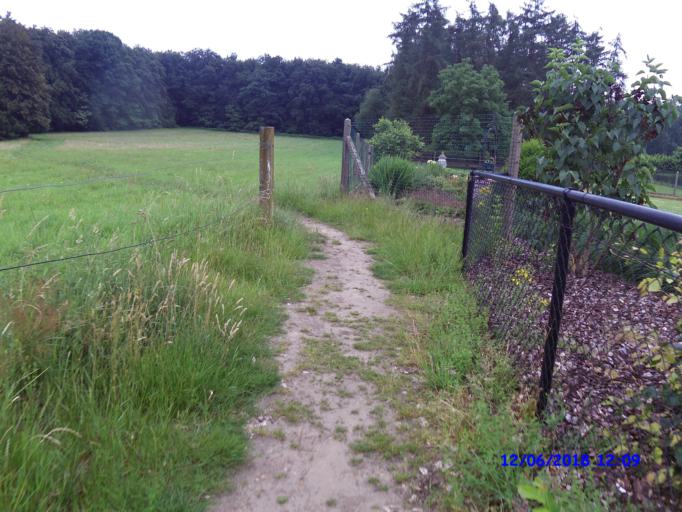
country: BE
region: Flanders
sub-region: Provincie Vlaams-Brabant
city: Oud-Heverlee
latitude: 50.8332
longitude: 4.6633
